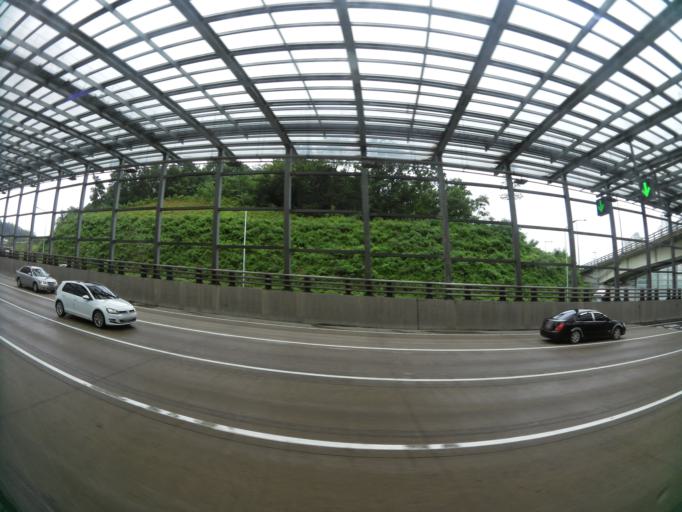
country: KR
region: Gyeonggi-do
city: Suwon-si
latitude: 37.2927
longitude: 127.0809
